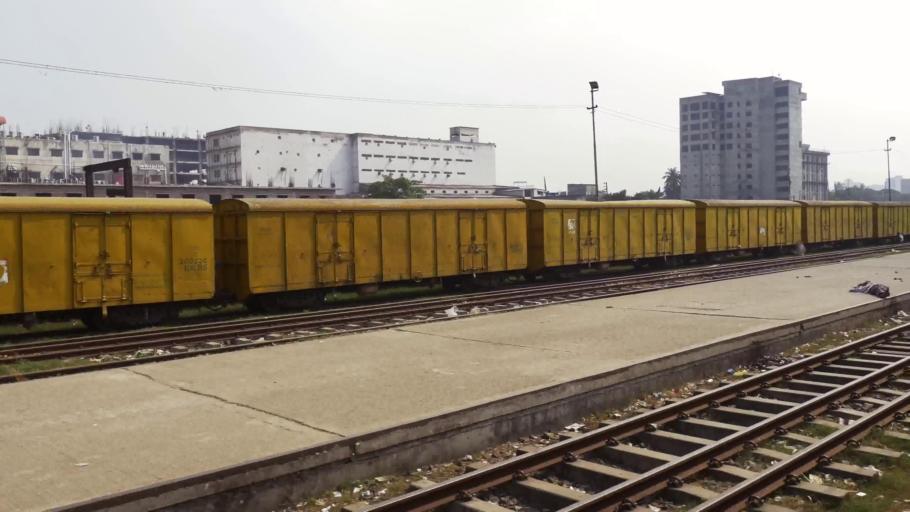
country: BD
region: Dhaka
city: Paltan
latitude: 23.7950
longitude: 90.4005
